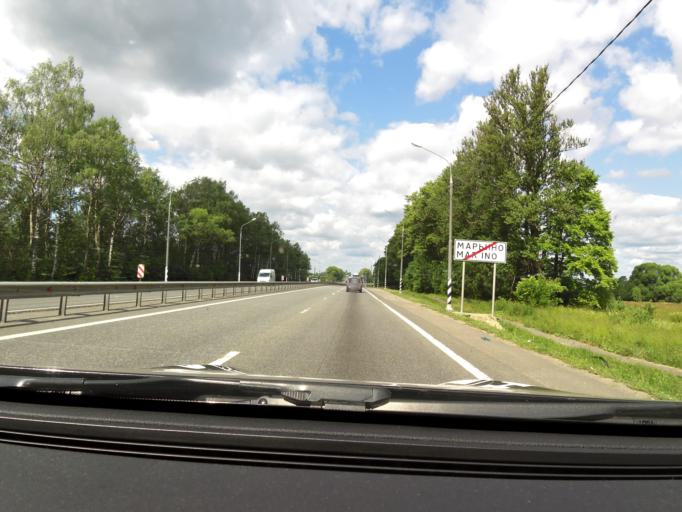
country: RU
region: Tverskaya
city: Likhoslavl'
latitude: 56.9795
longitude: 35.2579
